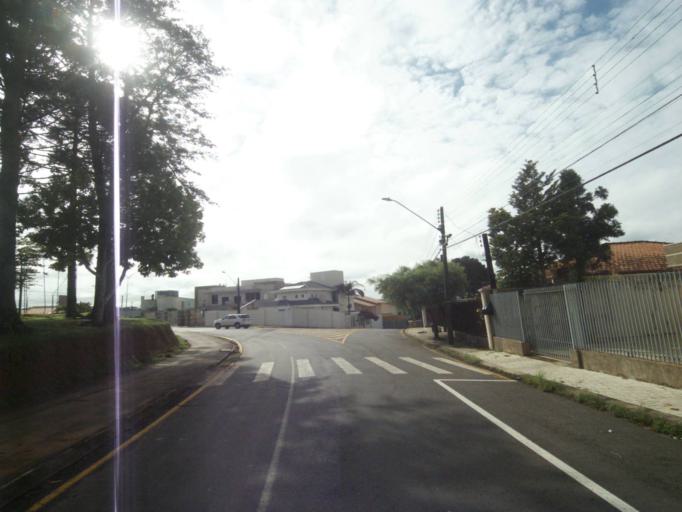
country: BR
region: Parana
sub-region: Telemaco Borba
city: Telemaco Borba
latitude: -24.3331
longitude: -50.6090
